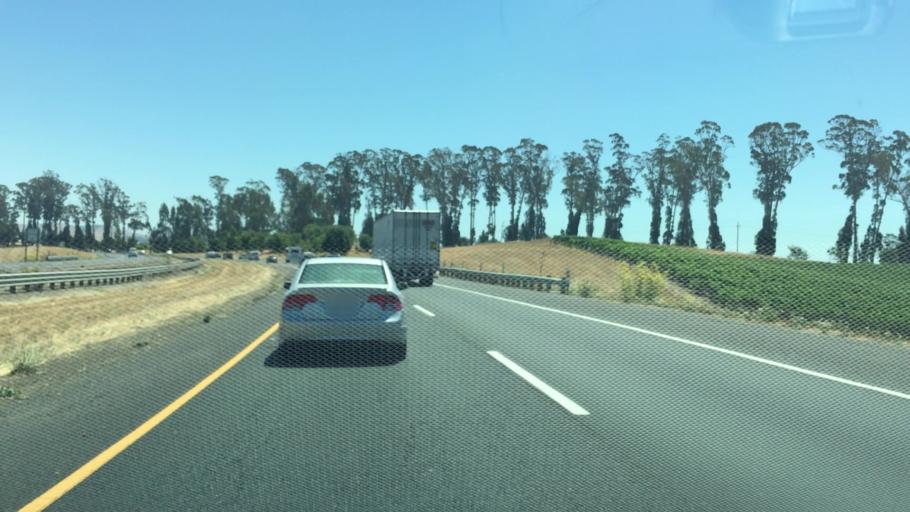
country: US
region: California
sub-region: Napa County
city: Napa
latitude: 38.2506
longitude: -122.3028
